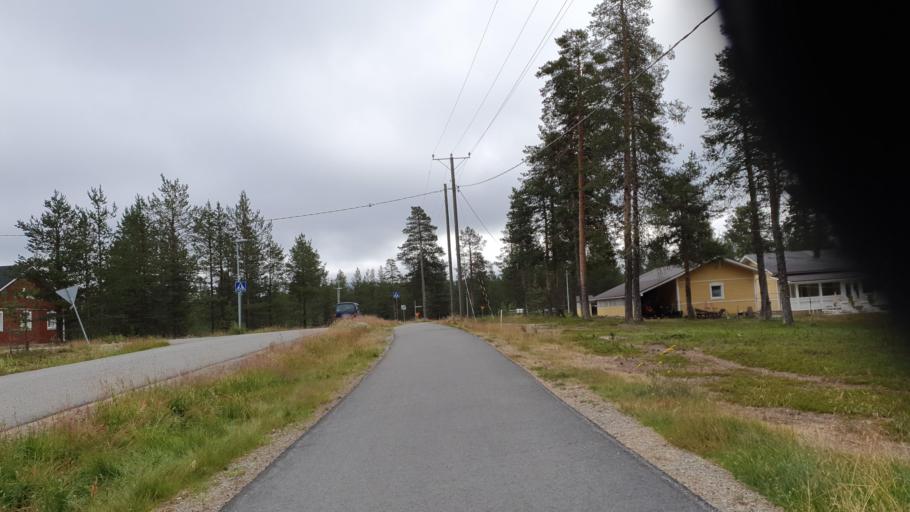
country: FI
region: Lapland
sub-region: Tunturi-Lappi
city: Kolari
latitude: 67.6237
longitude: 24.1505
